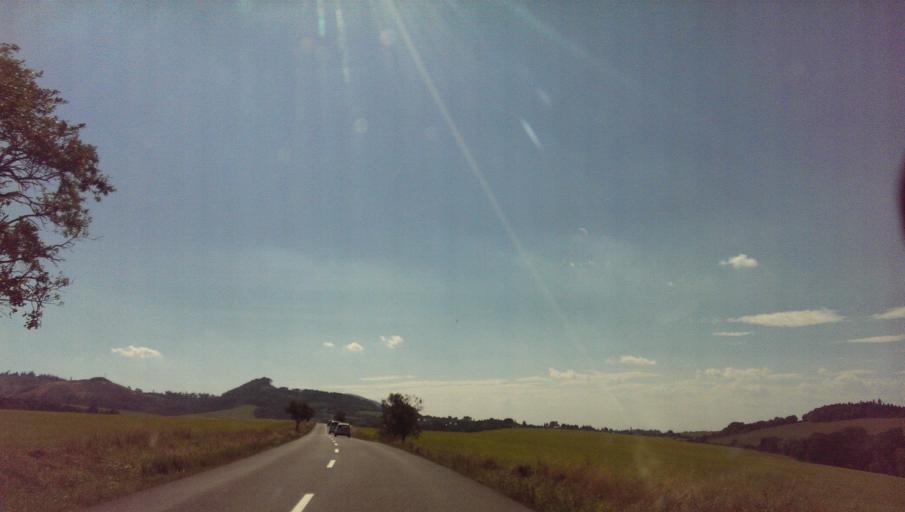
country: CZ
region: Zlin
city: Kelc
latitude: 49.4469
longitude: 17.8614
